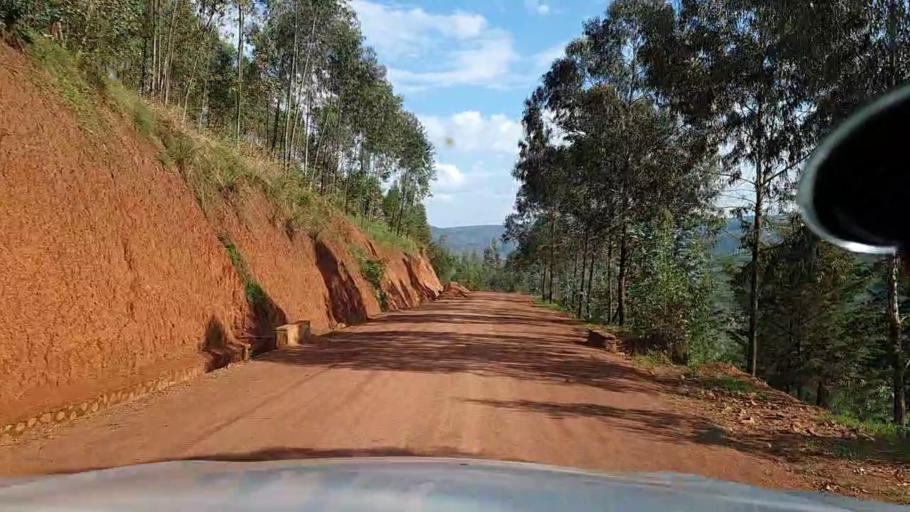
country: RW
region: Kigali
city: Kigali
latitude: -1.8397
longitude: 29.8558
